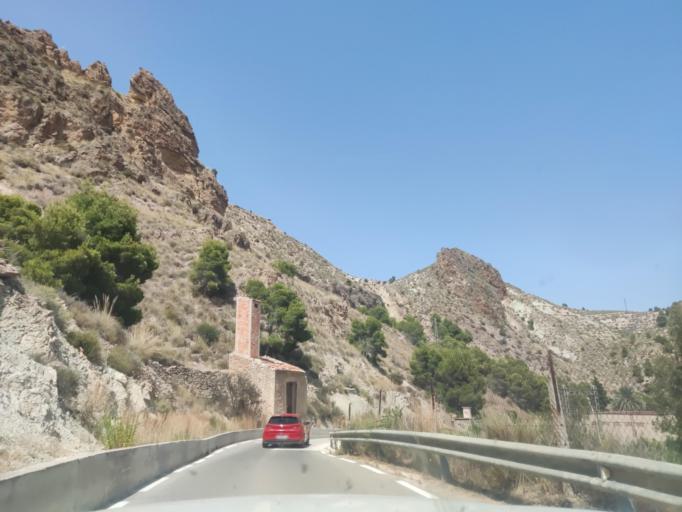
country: ES
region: Murcia
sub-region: Murcia
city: Archena
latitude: 38.1303
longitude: -1.3086
